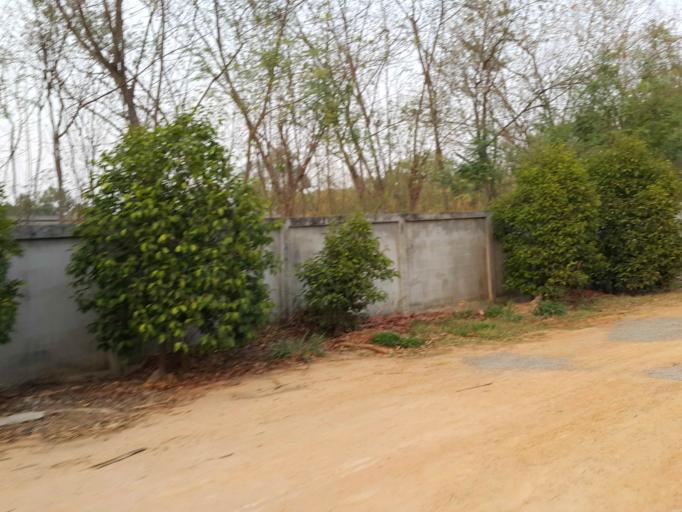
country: TH
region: Chiang Mai
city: San Sai
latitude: 18.9136
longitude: 99.0137
